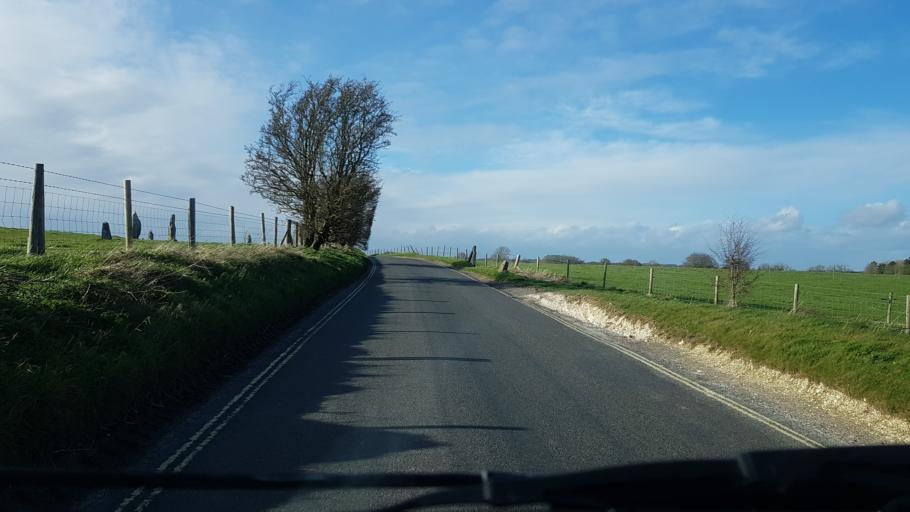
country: GB
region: England
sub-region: Wiltshire
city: Avebury
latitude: 51.4244
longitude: -1.8493
